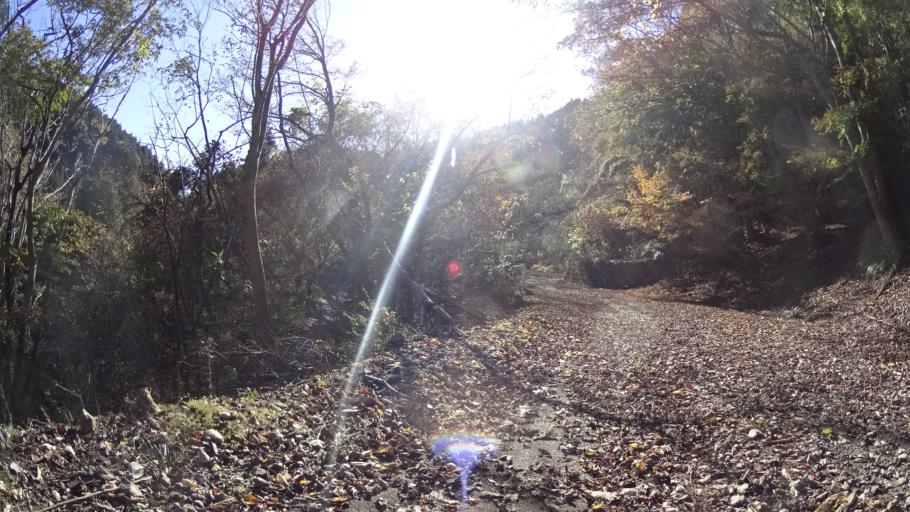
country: JP
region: Kanagawa
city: Atsugi
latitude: 35.5087
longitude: 139.2677
